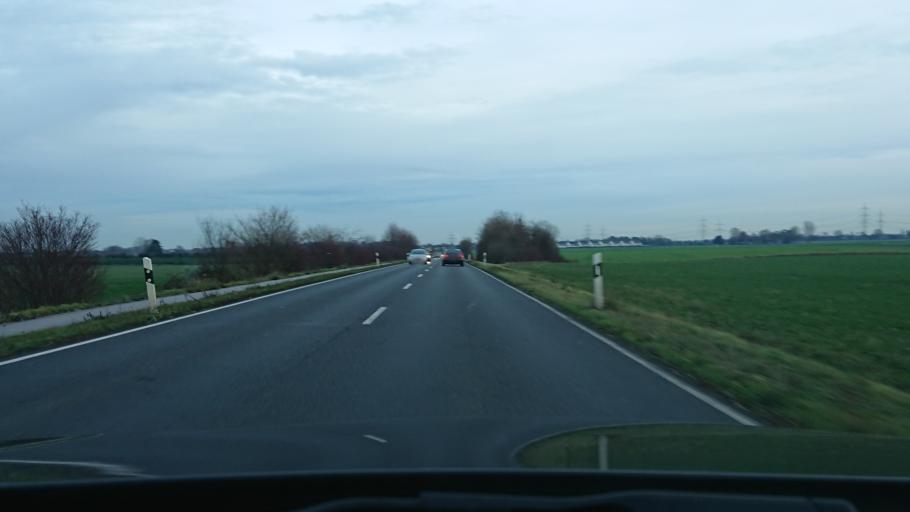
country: DE
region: North Rhine-Westphalia
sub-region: Regierungsbezirk Koln
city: Sinnersdorf
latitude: 51.0231
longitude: 6.7957
